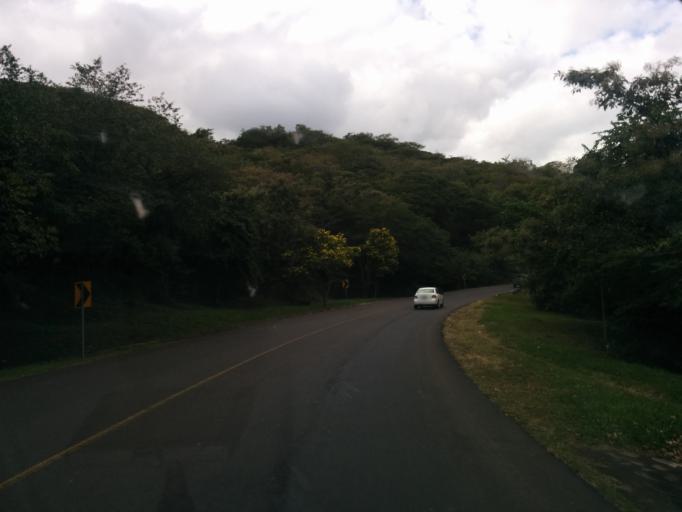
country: NI
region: Esteli
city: Esteli
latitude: 12.9959
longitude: -86.2836
